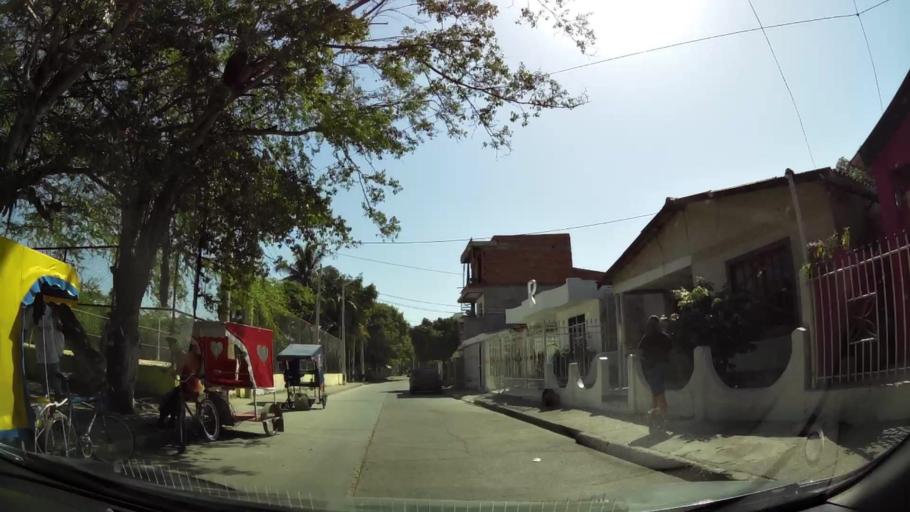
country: CO
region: Bolivar
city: Cartagena
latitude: 10.4422
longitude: -75.5184
